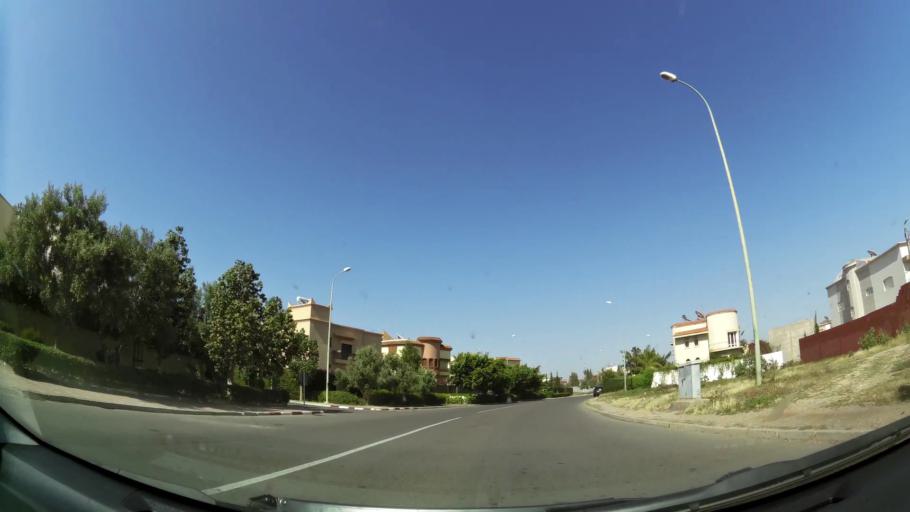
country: MA
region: Souss-Massa-Draa
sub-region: Inezgane-Ait Mellou
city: Inezgane
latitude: 30.3623
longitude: -9.5494
